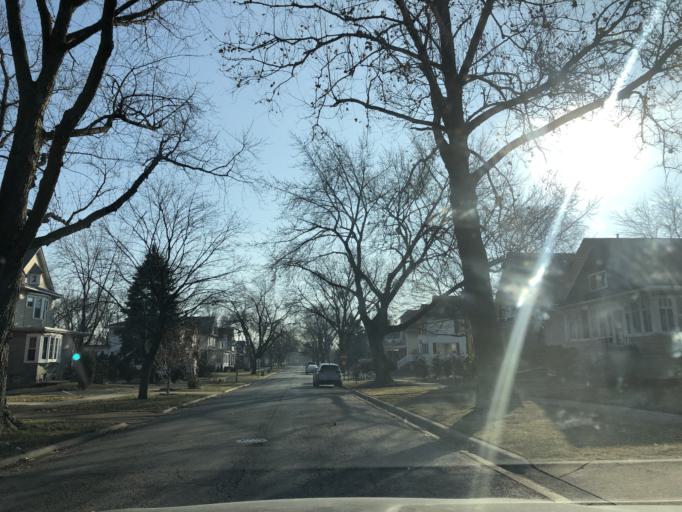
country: US
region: Illinois
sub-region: Cook County
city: Maywood
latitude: 41.8742
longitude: -87.8375
